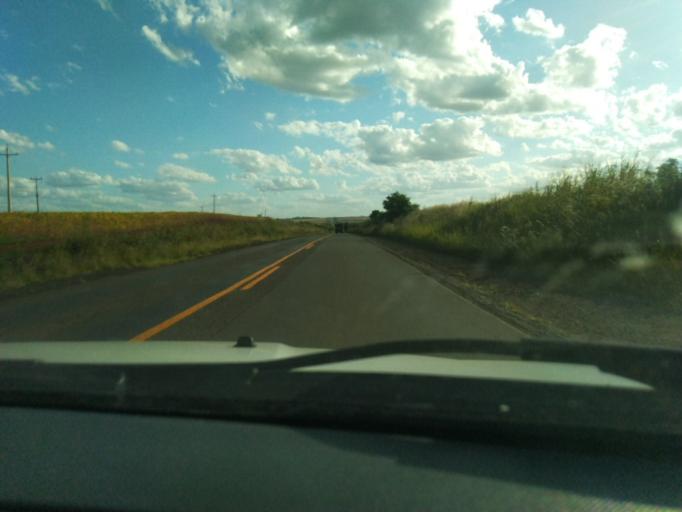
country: AR
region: Corrientes
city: Garruchos
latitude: -28.5524
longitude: -55.5696
